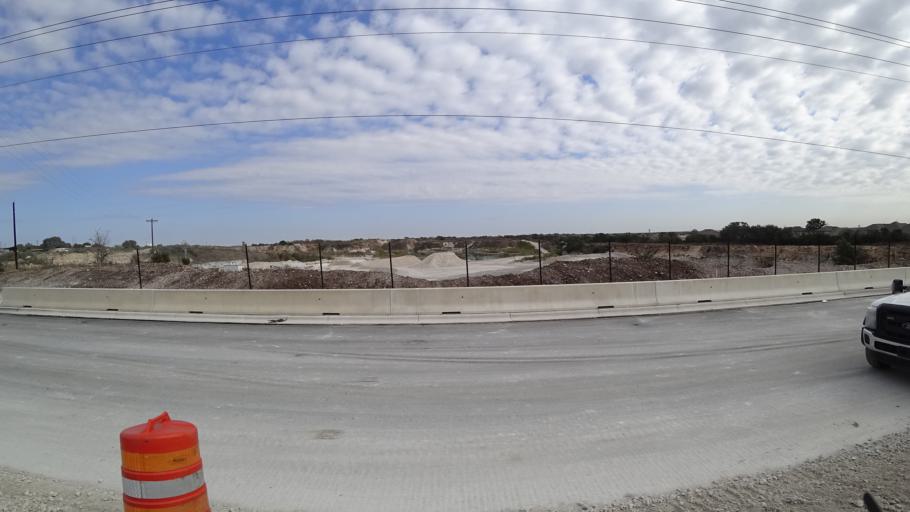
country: US
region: Texas
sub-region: Williamson County
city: Cedar Park
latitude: 30.4983
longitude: -97.8574
